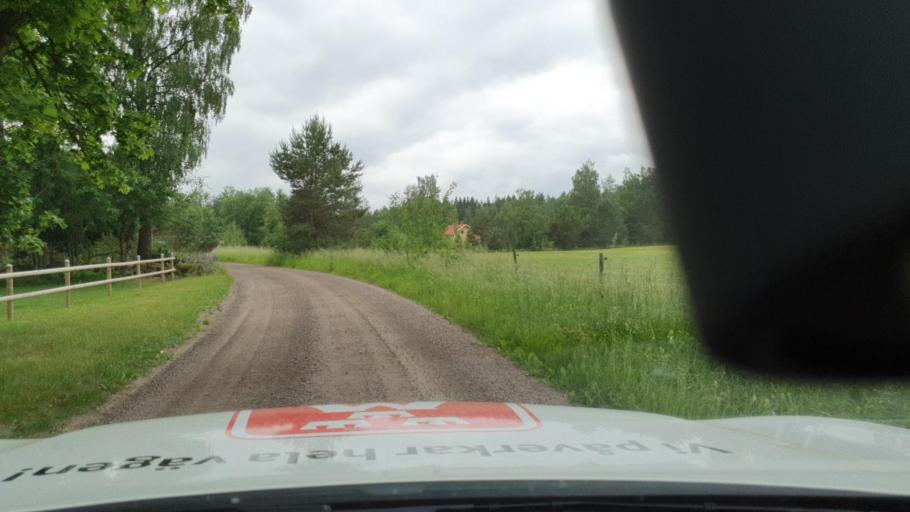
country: SE
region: Vaestra Goetaland
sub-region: Hjo Kommun
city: Hjo
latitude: 58.3450
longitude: 14.2929
